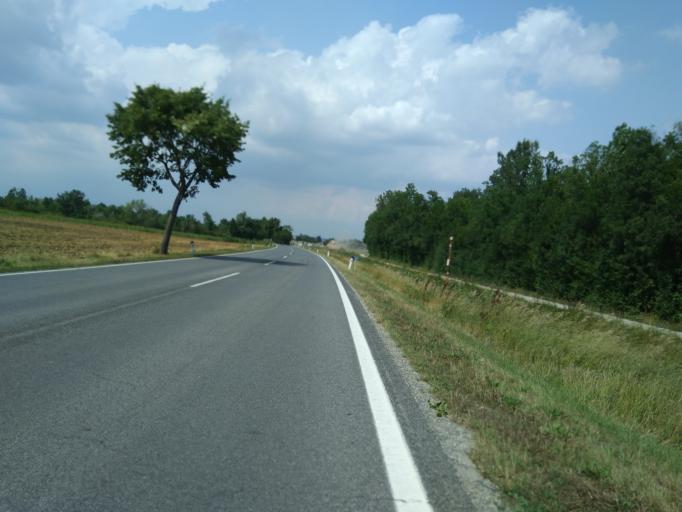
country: AT
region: Lower Austria
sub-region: Politischer Bezirk Ganserndorf
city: Ganserndorf
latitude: 48.3518
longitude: 16.7101
